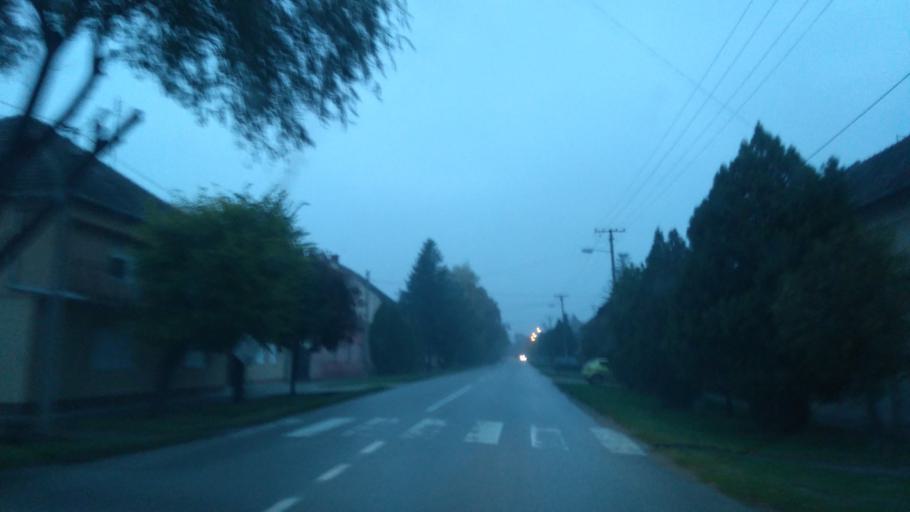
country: RS
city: Backo Petrovo Selo
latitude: 45.7058
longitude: 20.0870
